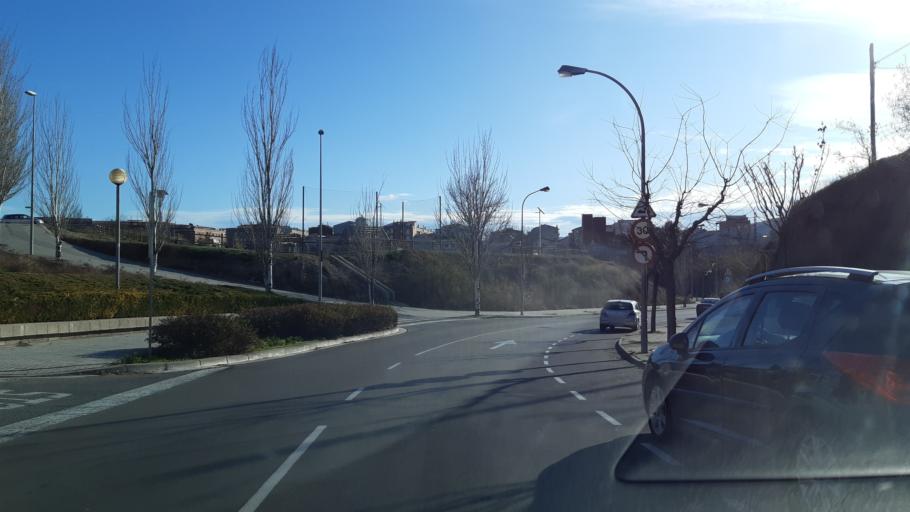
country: ES
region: Catalonia
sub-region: Provincia de Barcelona
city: Vilanova del Cami
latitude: 41.5745
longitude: 1.6322
